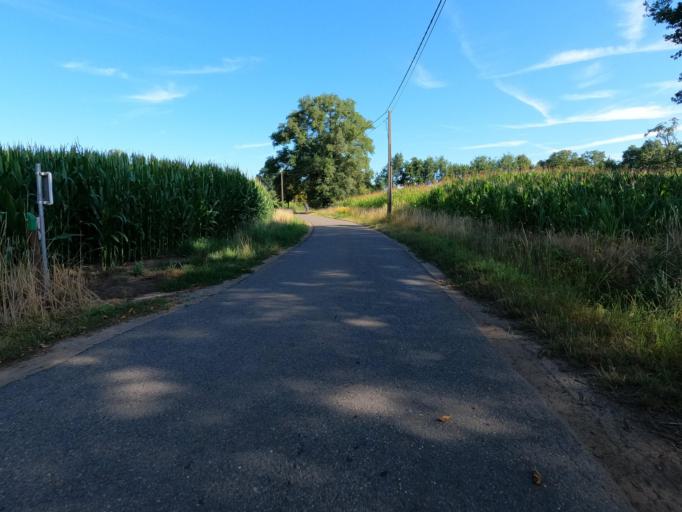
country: BE
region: Flanders
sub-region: Provincie Antwerpen
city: Herenthout
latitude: 51.1571
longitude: 4.7360
